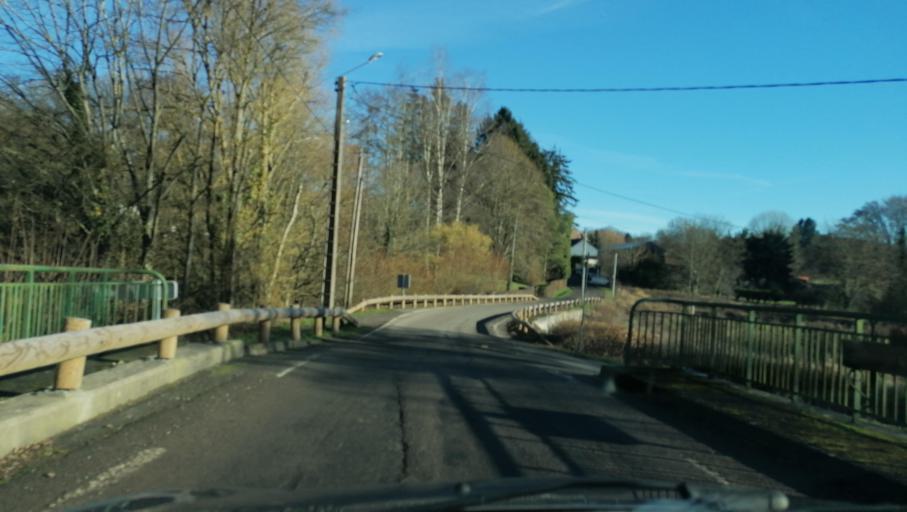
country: FR
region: Nord-Pas-de-Calais
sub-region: Departement du Nord
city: Recquignies
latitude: 50.2052
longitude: 4.0666
